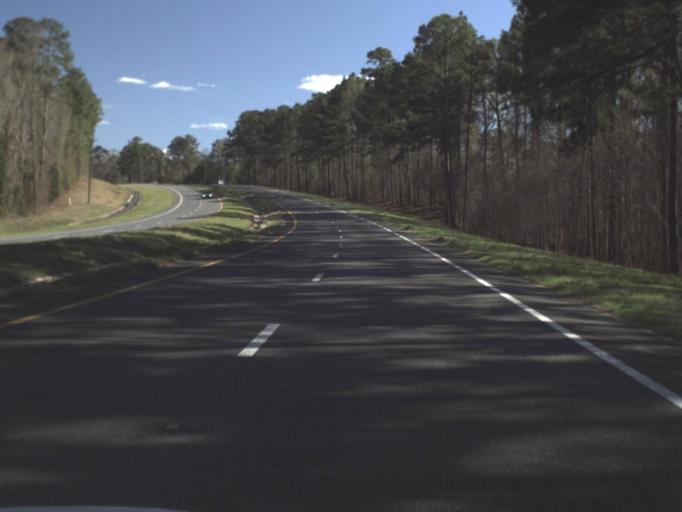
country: US
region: Florida
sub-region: Gadsden County
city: Midway
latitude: 30.5203
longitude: -84.4677
